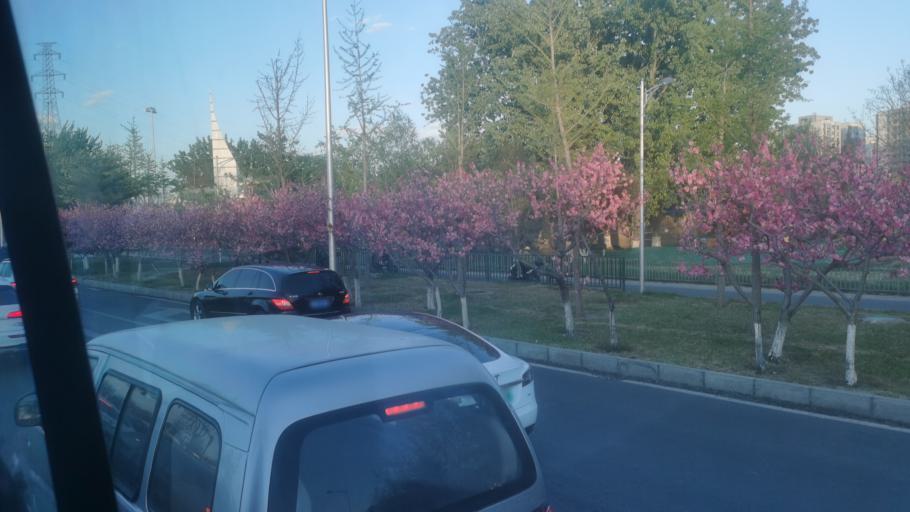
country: CN
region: Beijing
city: Xibeiwang
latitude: 40.0801
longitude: 116.2590
